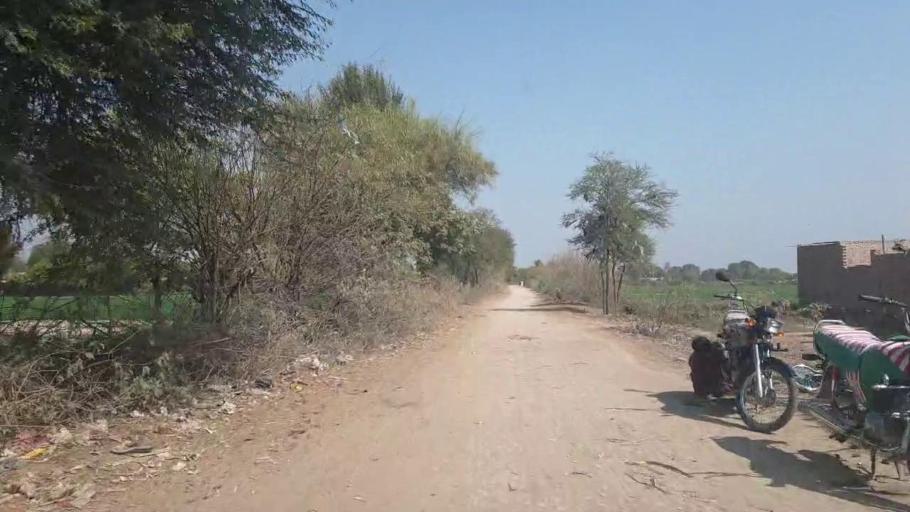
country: PK
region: Sindh
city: Tando Allahyar
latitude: 25.4286
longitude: 68.8368
